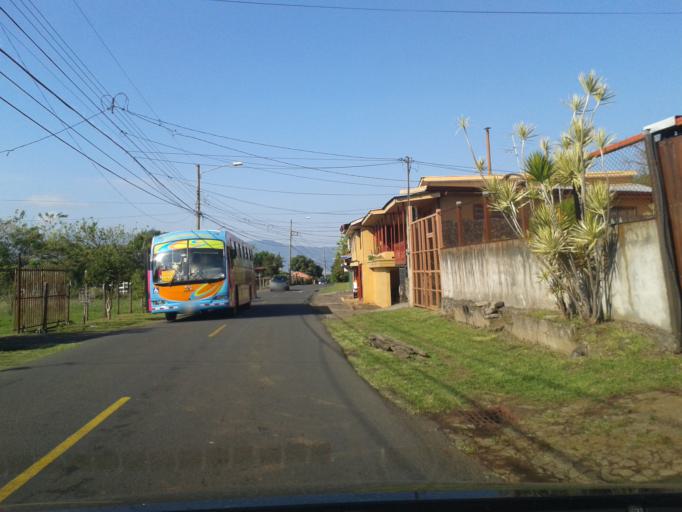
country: CR
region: Heredia
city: Llorente
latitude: 10.0101
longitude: -84.1481
